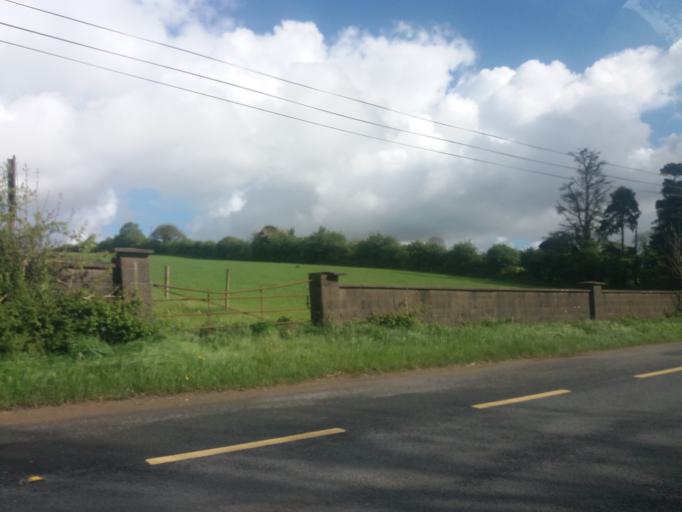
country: IE
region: Leinster
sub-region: Loch Garman
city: Ferns
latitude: 52.5943
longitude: -6.4858
